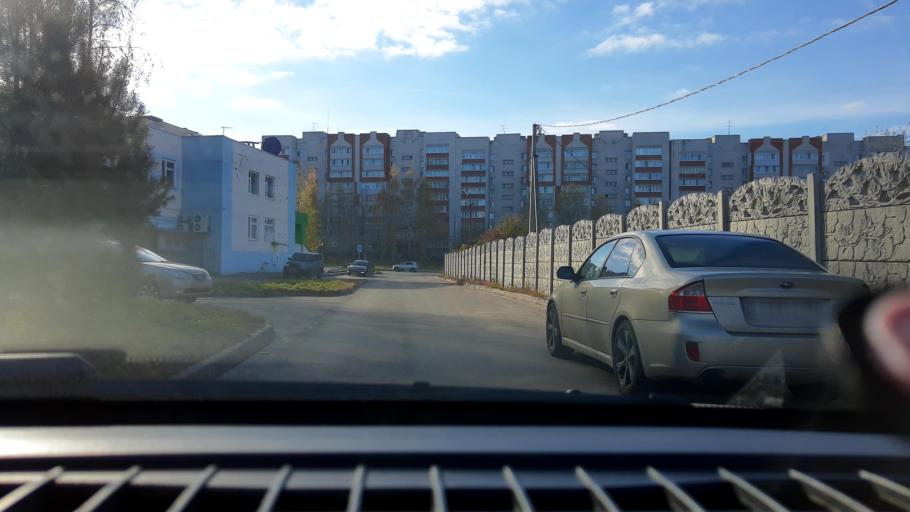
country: RU
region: Nizjnij Novgorod
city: Kstovo
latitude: 56.1592
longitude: 44.2097
